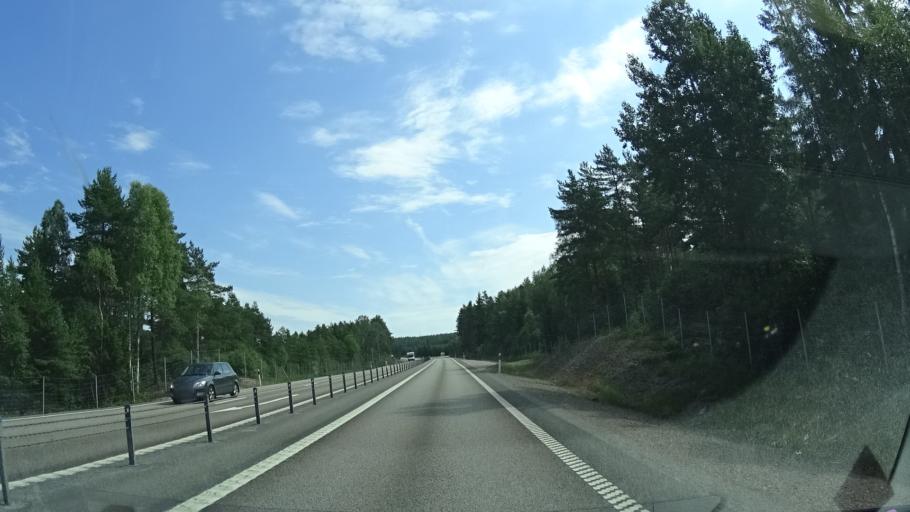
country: SE
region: Vaermland
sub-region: Kristinehamns Kommun
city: Kristinehamn
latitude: 59.3110
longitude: 14.1920
